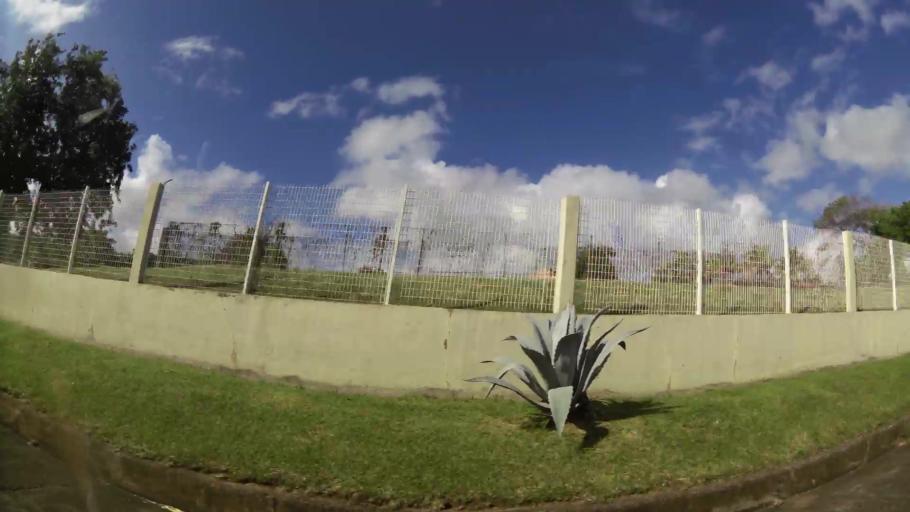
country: MQ
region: Martinique
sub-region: Martinique
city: Le Vauclin
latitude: 14.5582
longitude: -60.8476
